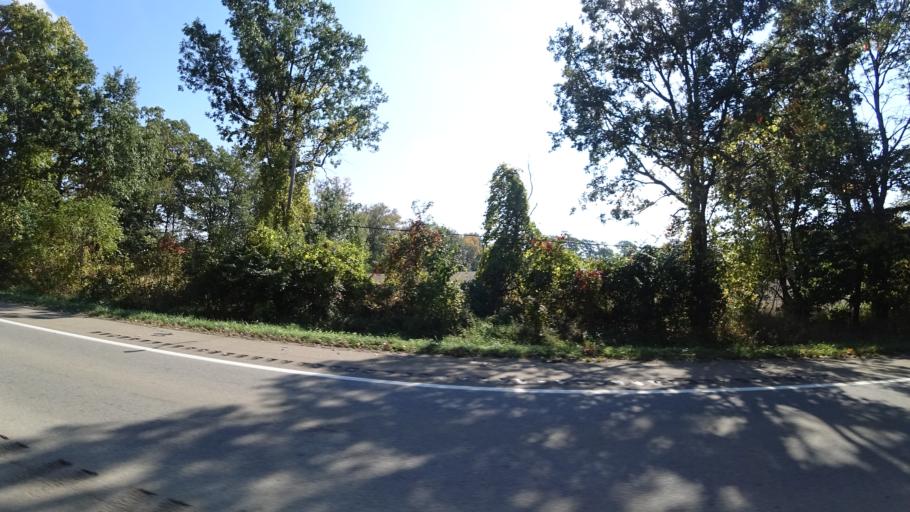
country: US
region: Michigan
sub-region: Jackson County
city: Spring Arbor
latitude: 42.1970
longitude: -84.5898
